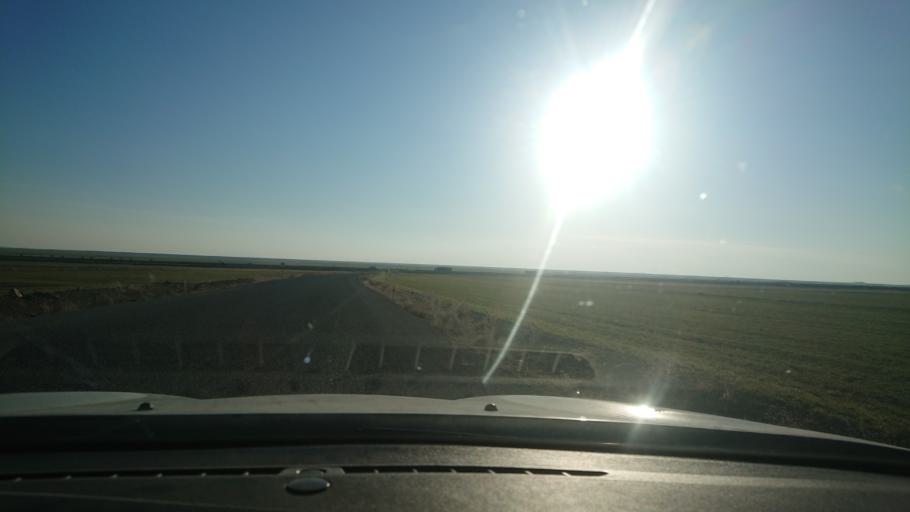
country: TR
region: Aksaray
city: Acipinar
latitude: 38.6653
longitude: 33.7196
